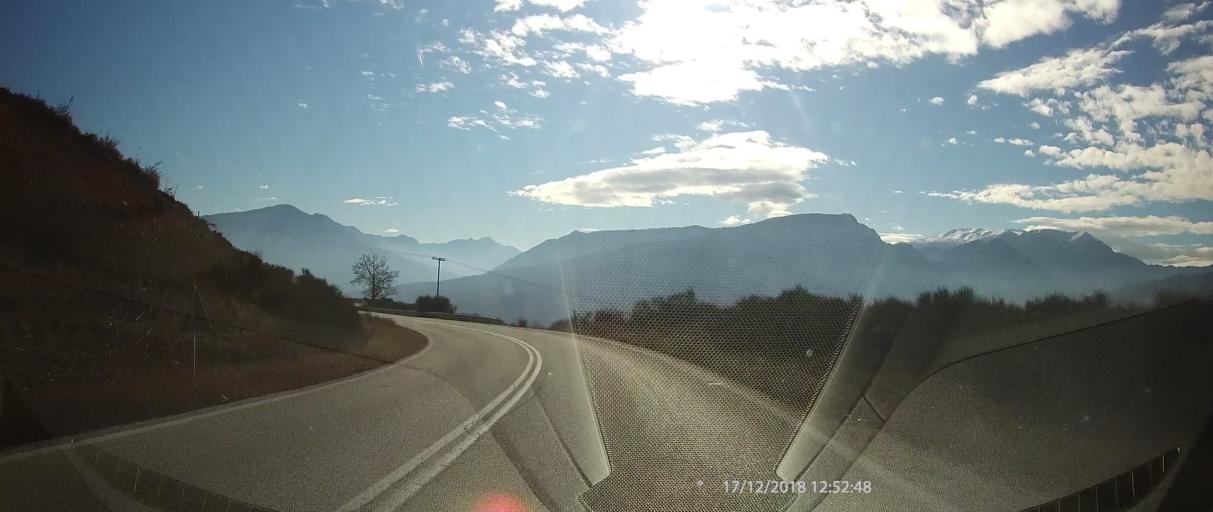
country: GR
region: Thessaly
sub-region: Trikala
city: Kastraki
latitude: 39.7574
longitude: 21.4829
